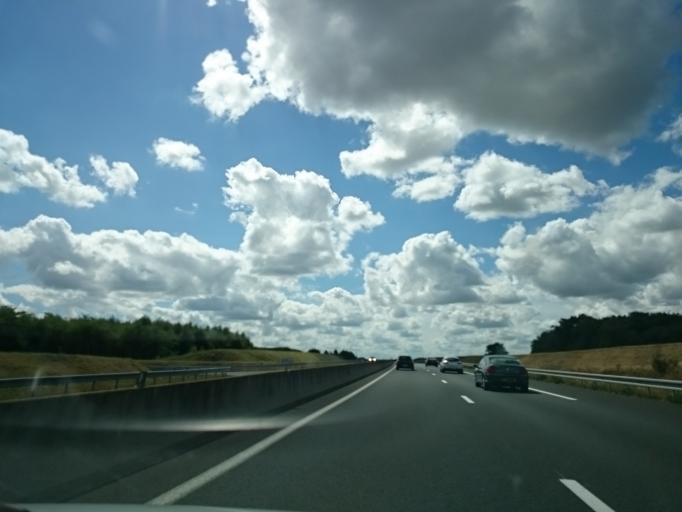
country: FR
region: Pays de la Loire
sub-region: Departement de Maine-et-Loire
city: Saint-Lambert-la-Potherie
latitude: 47.4886
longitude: -0.6545
